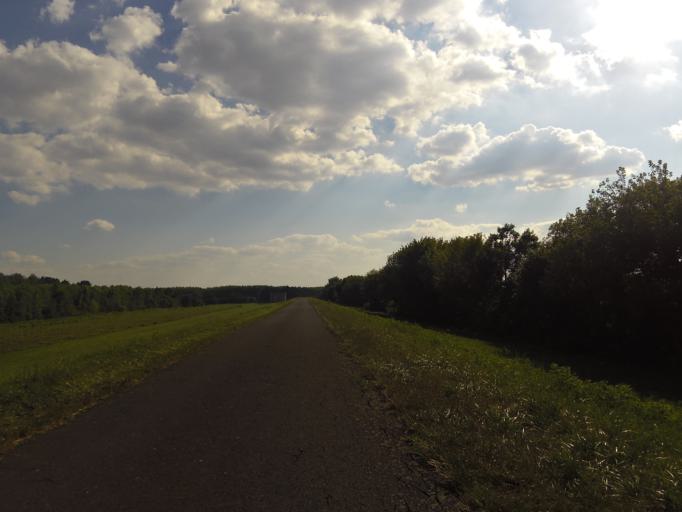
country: HU
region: Jasz-Nagykun-Szolnok
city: Abadszalok
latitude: 47.5288
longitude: 20.6095
